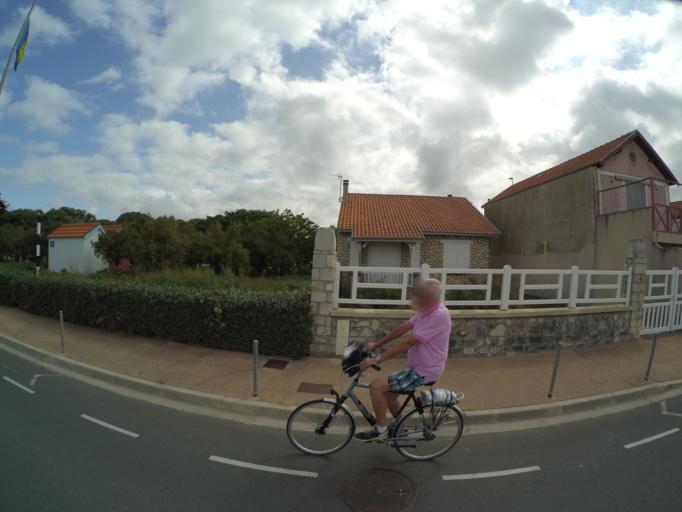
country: FR
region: Poitou-Charentes
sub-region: Departement de la Charente-Maritime
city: Chatelaillon-Plage
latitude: 46.0827
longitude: -1.0959
